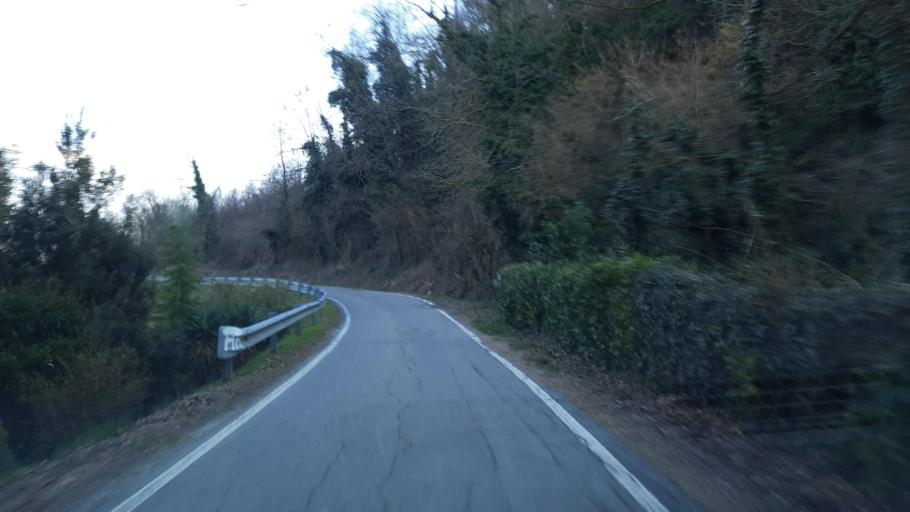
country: IT
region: Piedmont
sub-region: Provincia di Alessandria
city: Odalengo Grande
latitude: 45.1055
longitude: 8.1708
